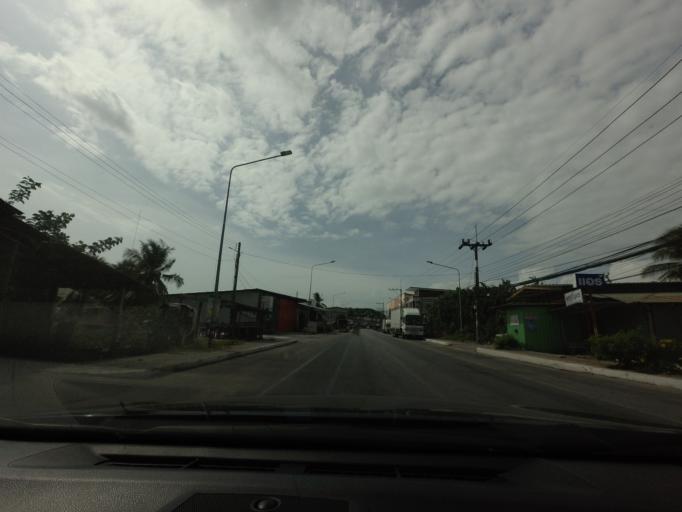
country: TH
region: Pattani
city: Pattani
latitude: 6.8757
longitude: 101.2484
